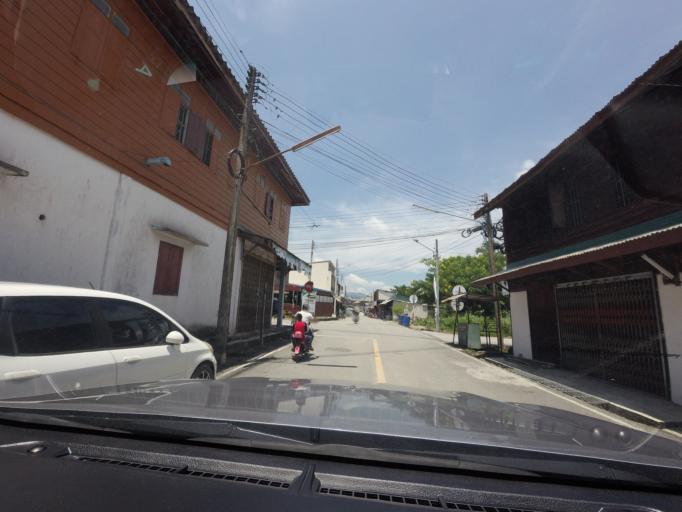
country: TH
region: Narathiwat
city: Rueso
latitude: 6.3944
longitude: 101.5159
